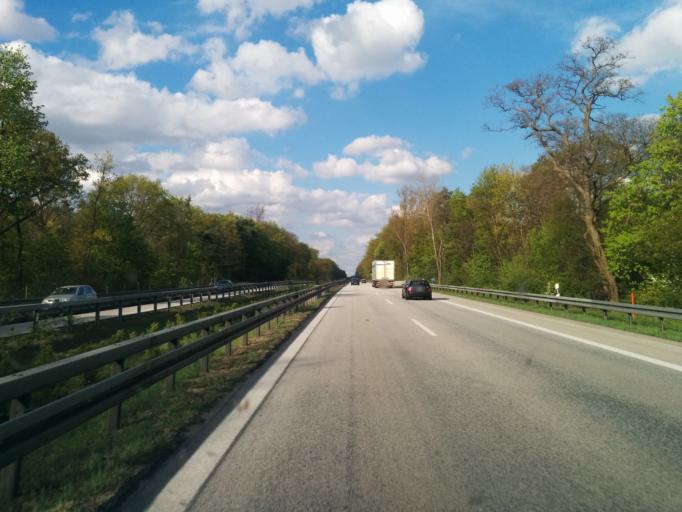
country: DE
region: Berlin
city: Nikolassee
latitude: 52.4529
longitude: 13.2159
